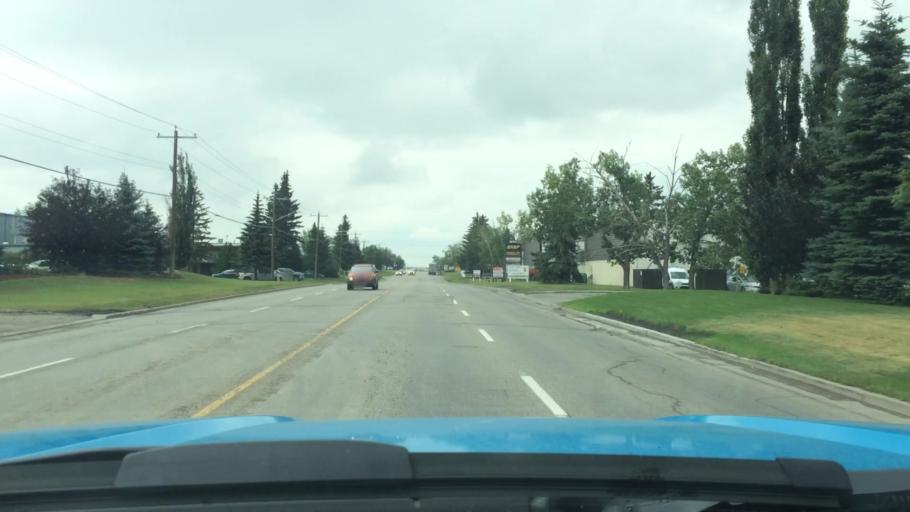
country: CA
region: Alberta
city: Calgary
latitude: 51.0859
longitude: -114.0116
